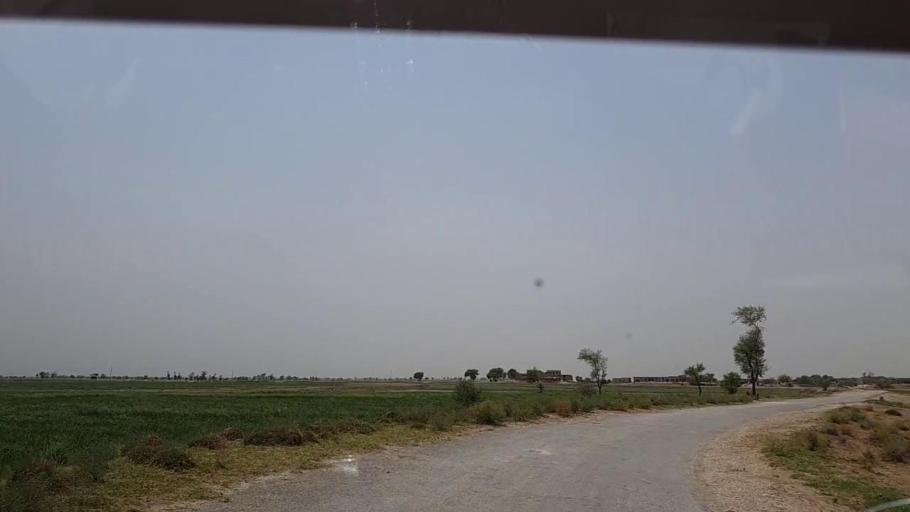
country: PK
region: Sindh
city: Khairpur Nathan Shah
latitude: 27.0173
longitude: 67.6620
